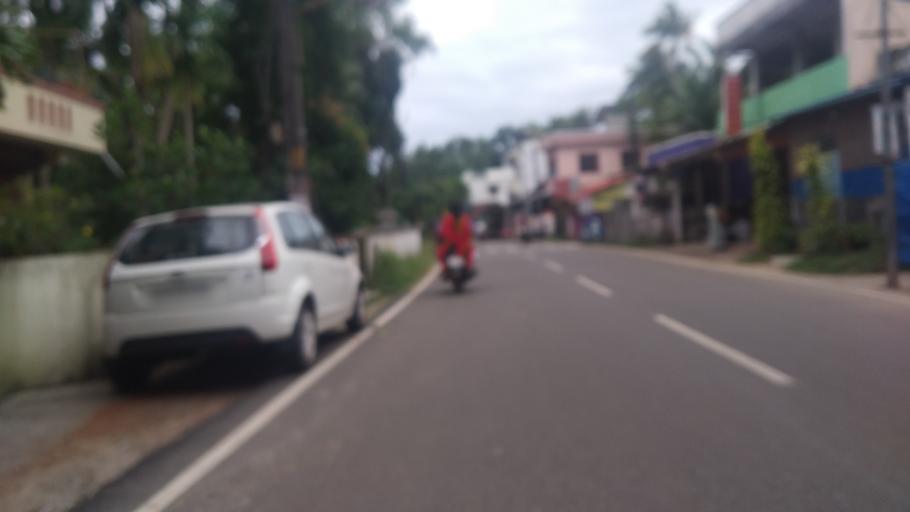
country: IN
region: Kerala
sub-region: Alappuzha
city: Arukutti
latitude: 9.8656
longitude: 76.2916
